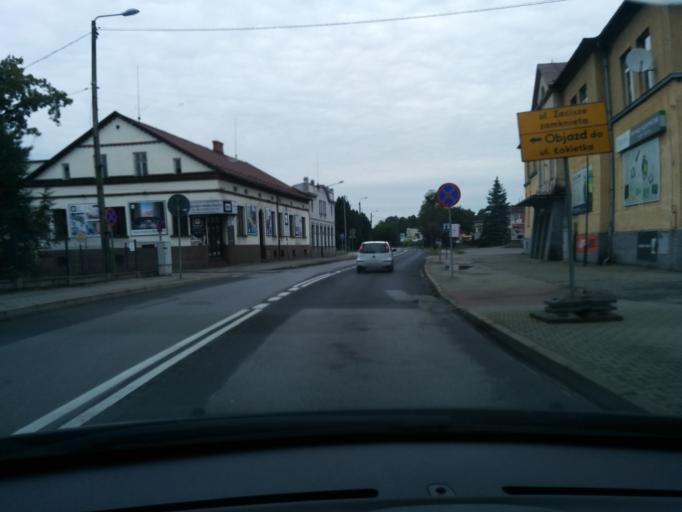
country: PL
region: Lesser Poland Voivodeship
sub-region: Powiat oswiecimski
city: Kety
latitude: 49.8849
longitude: 19.2201
